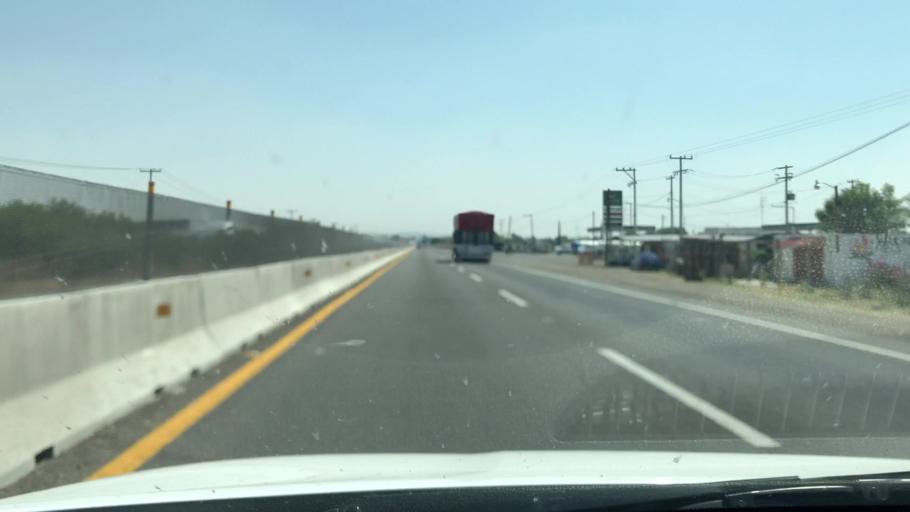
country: MX
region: Guanajuato
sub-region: Abasolo
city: San Bernardo Pena Blanca
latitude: 20.4740
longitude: -101.5014
